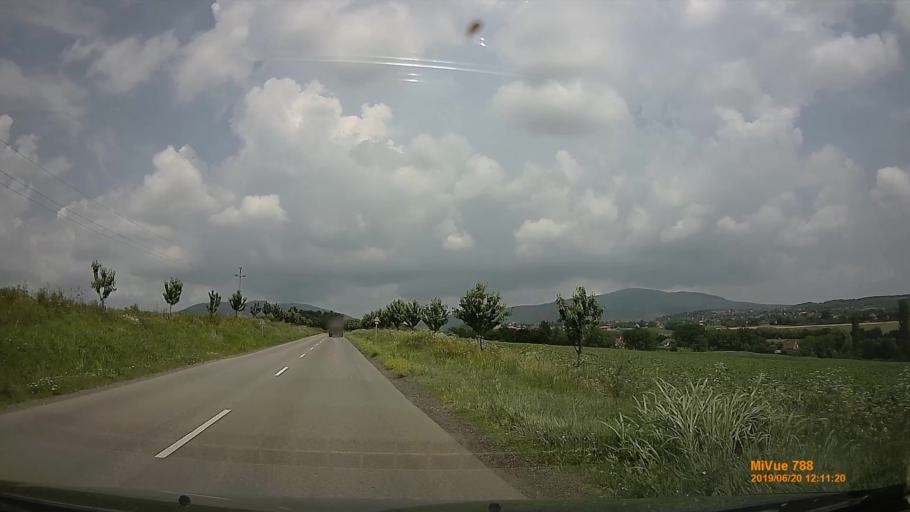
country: HU
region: Baranya
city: Hosszuheteny
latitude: 46.1356
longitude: 18.3480
